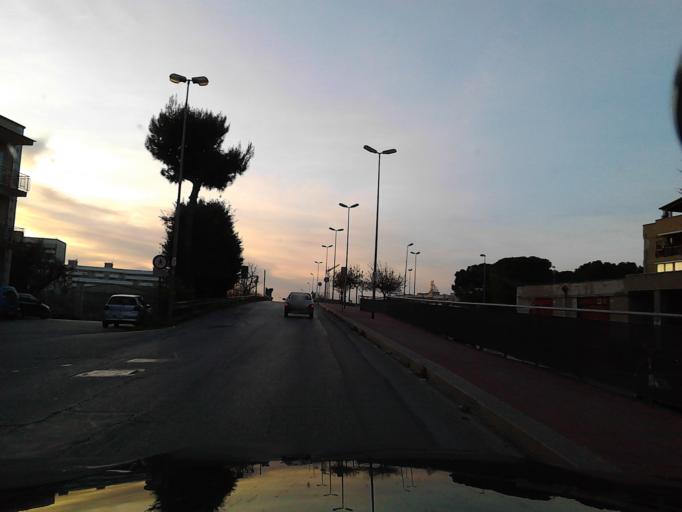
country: IT
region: Apulia
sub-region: Provincia di Bari
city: Valenzano
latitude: 41.0404
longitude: 16.8806
